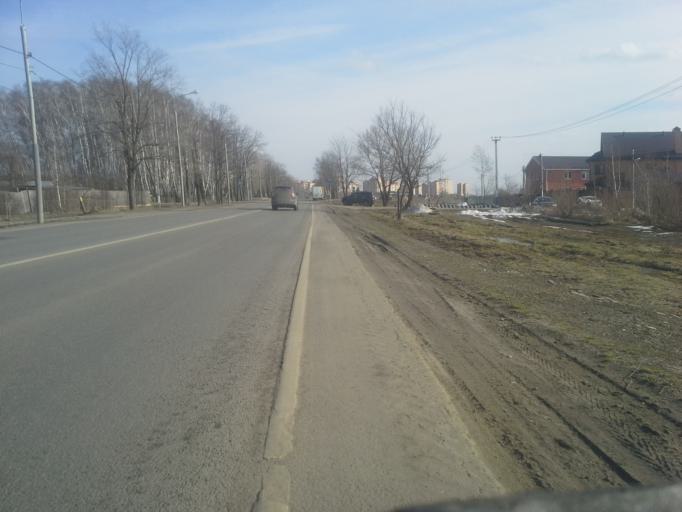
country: RU
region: Moskovskaya
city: Shcherbinka
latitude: 55.4795
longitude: 37.5253
